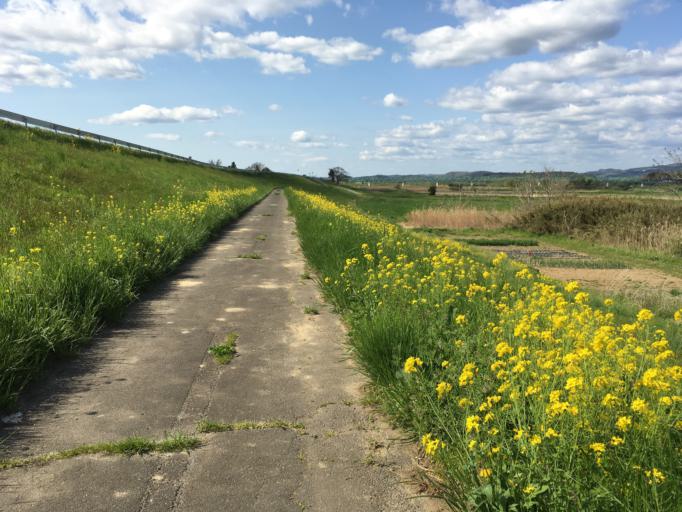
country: JP
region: Miyagi
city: Wakuya
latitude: 38.7137
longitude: 141.2651
